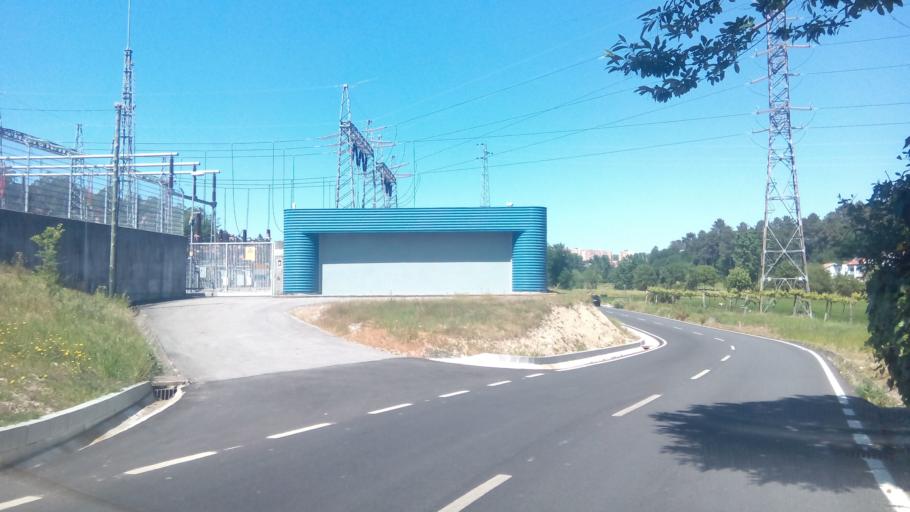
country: PT
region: Porto
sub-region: Paredes
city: Casteloes de Cepeda
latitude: 41.1896
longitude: -8.3375
